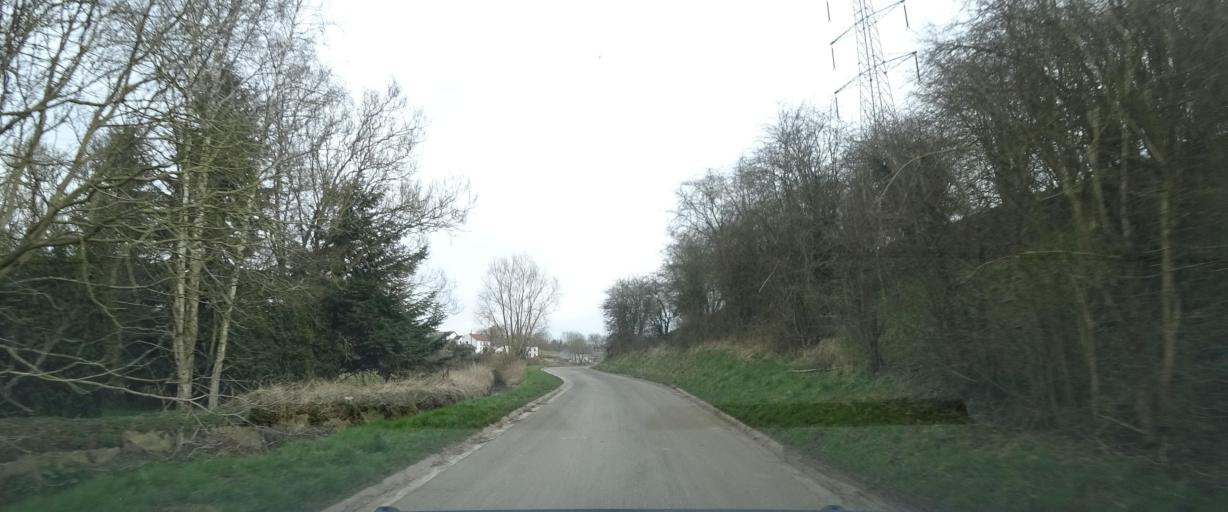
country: BE
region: Wallonia
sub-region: Province de Namur
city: Sombreffe
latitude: 50.4945
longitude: 4.6290
